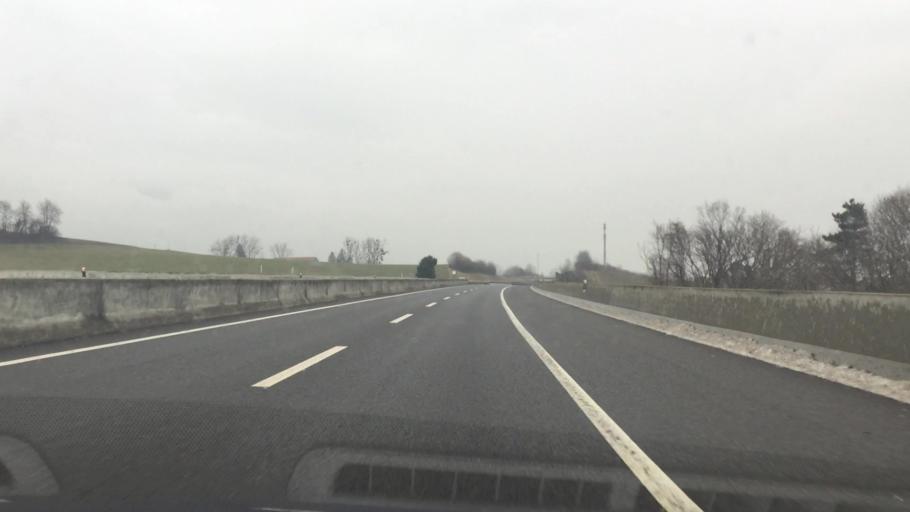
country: CH
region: Vaud
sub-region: Jura-Nord vaudois District
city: Grandson
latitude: 46.8074
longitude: 6.6296
